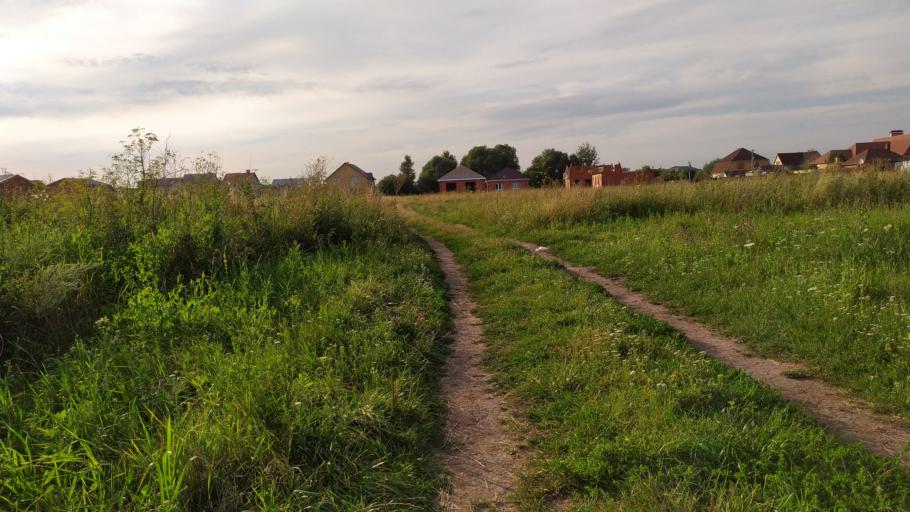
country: RU
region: Kursk
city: Kursk
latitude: 51.6417
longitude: 36.1588
